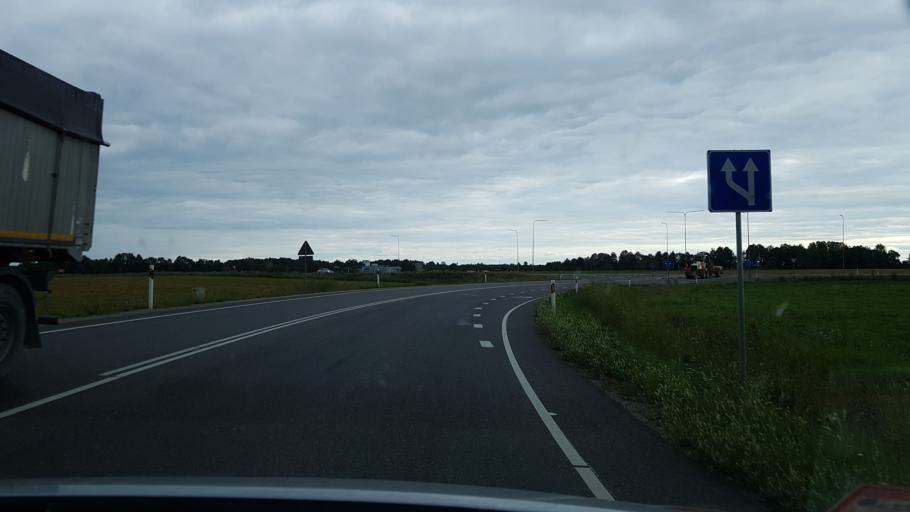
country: EE
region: Tartu
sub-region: Tartu linn
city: Tartu
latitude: 58.3688
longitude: 26.8844
